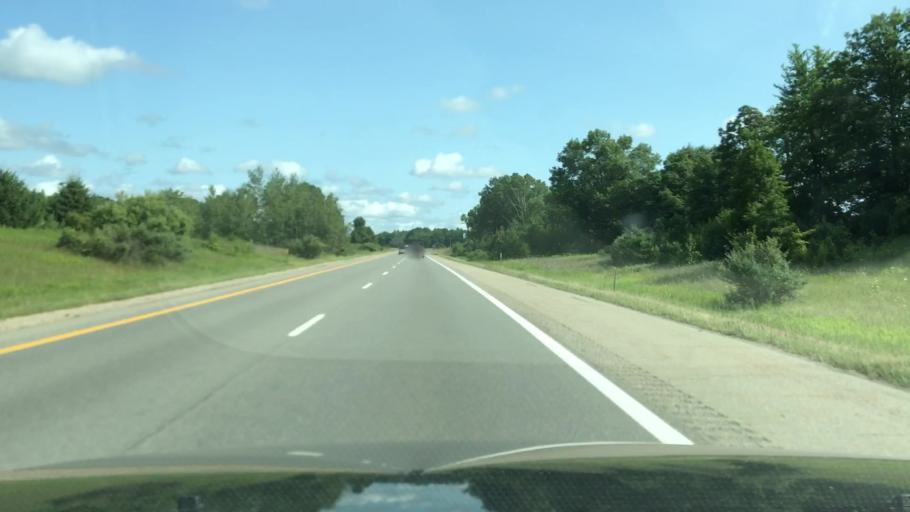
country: US
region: Michigan
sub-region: Kent County
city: Cedar Springs
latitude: 43.2705
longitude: -85.5418
